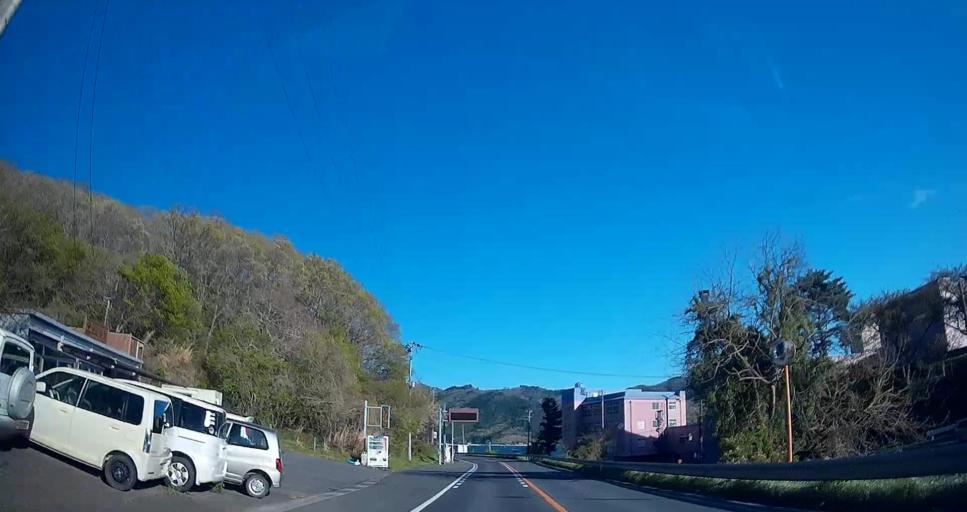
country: JP
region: Miyagi
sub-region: Oshika Gun
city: Onagawa Cho
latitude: 38.4345
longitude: 141.4096
